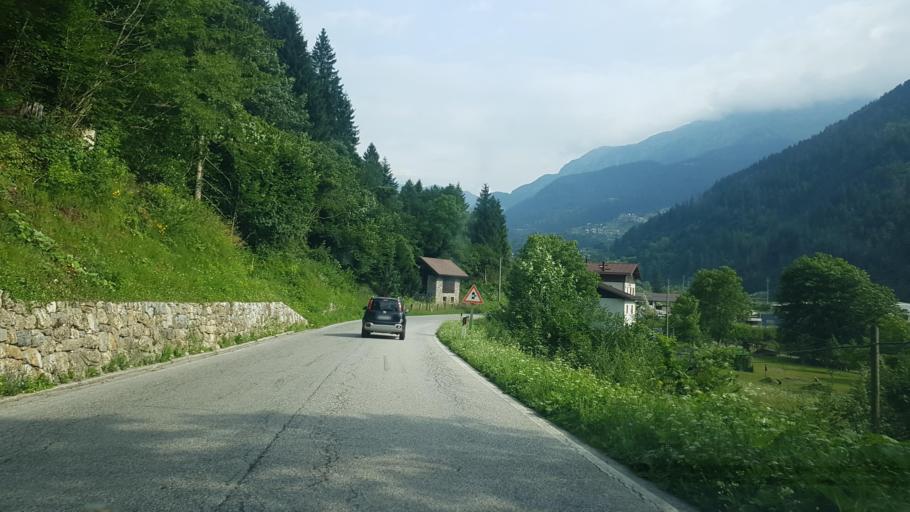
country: IT
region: Friuli Venezia Giulia
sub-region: Provincia di Udine
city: Paularo
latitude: 46.5154
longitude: 13.1226
